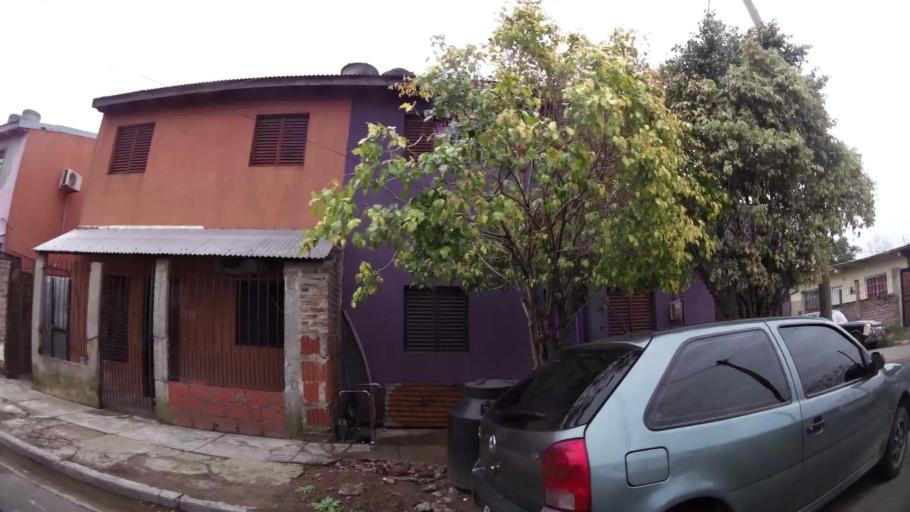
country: AR
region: Buenos Aires
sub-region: Partido de Lanus
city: Lanus
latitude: -34.7327
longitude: -58.3703
